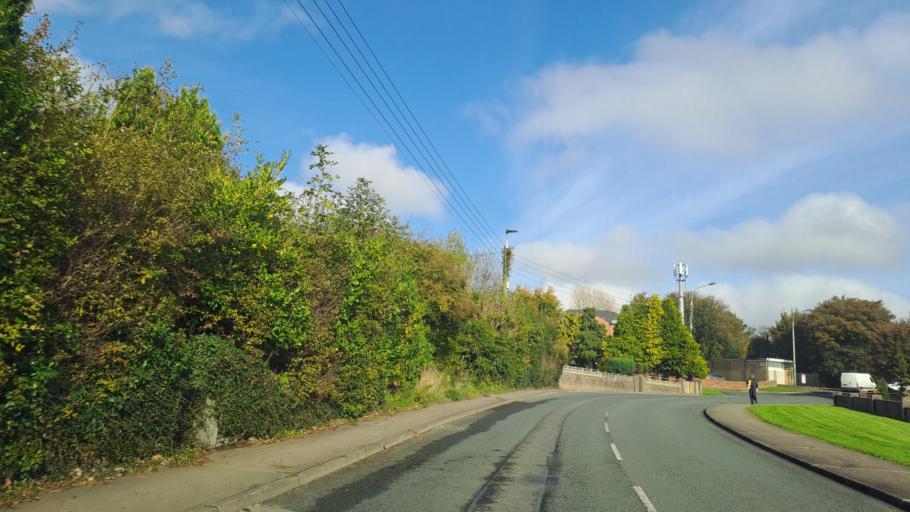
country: IE
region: Ulster
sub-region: An Cabhan
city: Cootehill
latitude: 54.0716
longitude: -7.0863
